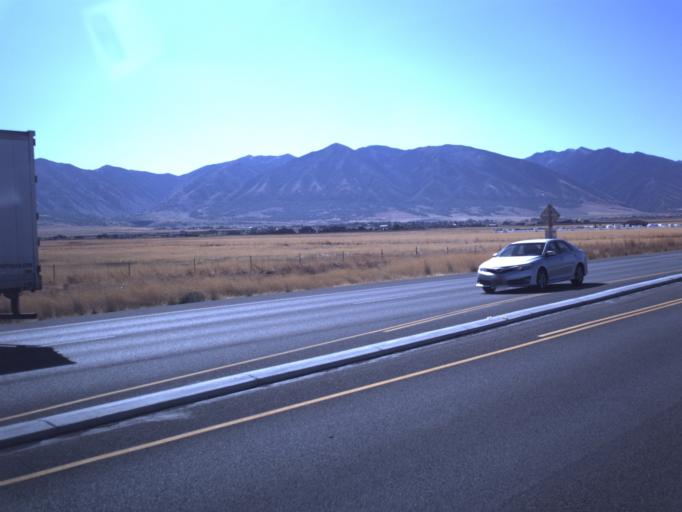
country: US
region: Utah
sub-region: Tooele County
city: Erda
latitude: 40.5999
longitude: -112.2943
